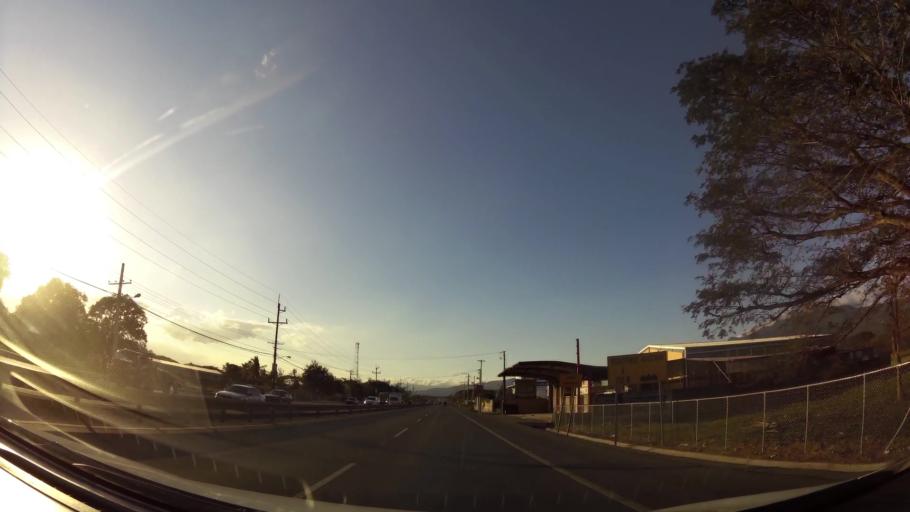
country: DO
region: Santiago
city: Palmar Arriba
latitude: 19.5086
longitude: -70.7556
